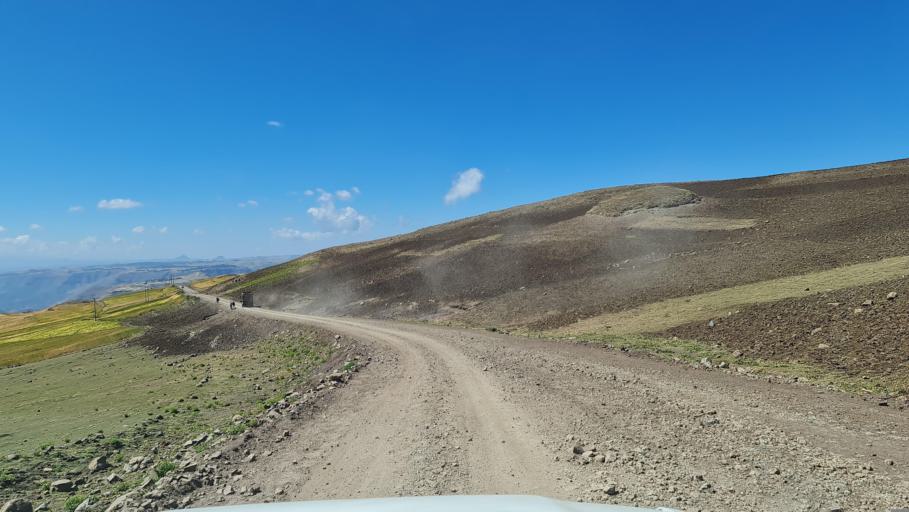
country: ET
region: Amhara
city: Debark'
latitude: 13.2366
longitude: 38.1103
